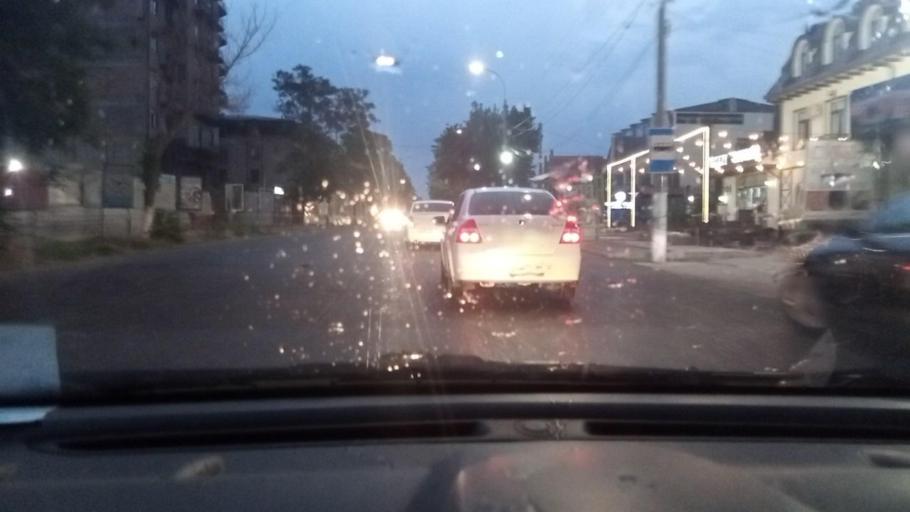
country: UZ
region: Toshkent
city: Salor
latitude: 41.3180
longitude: 69.3395
